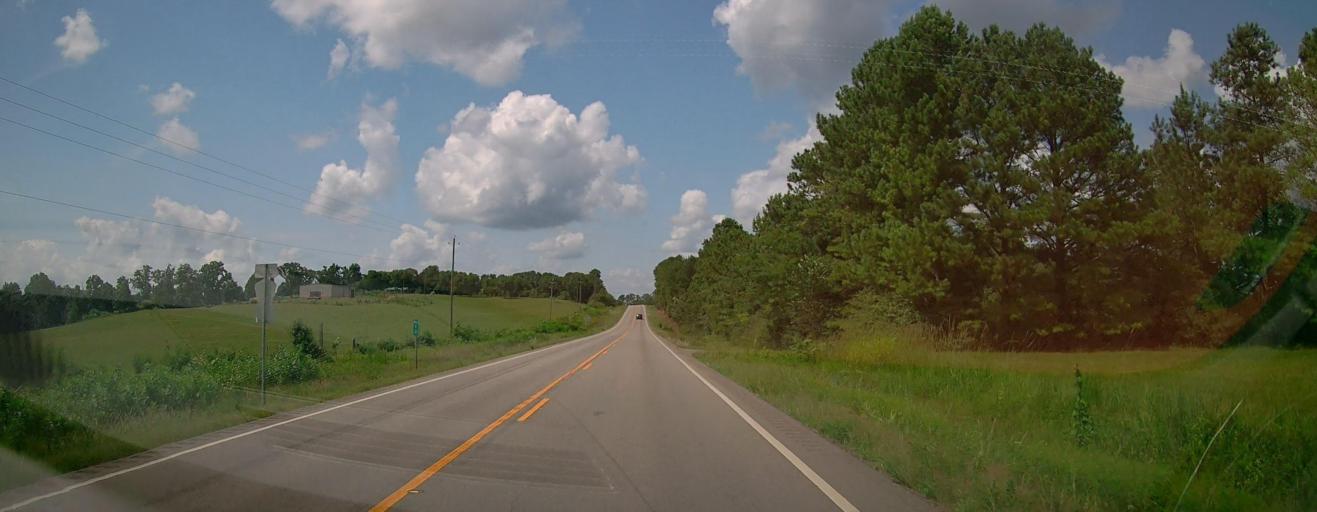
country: US
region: Alabama
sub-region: Cleburne County
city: Heflin
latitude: 33.5857
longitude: -85.4753
